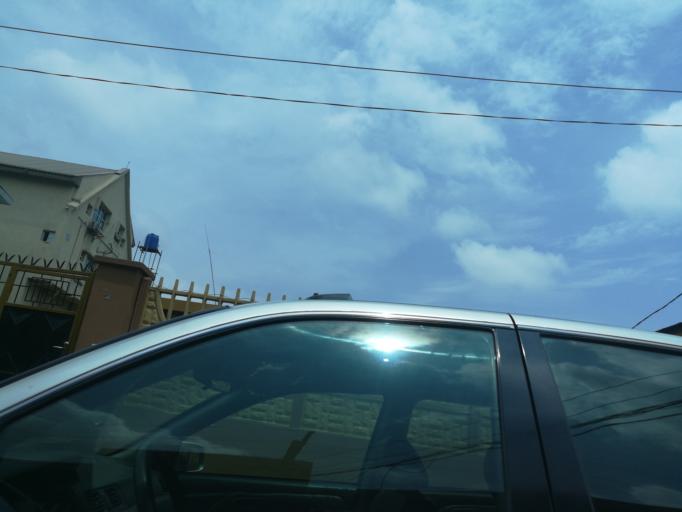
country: NG
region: Lagos
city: Ojota
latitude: 6.5898
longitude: 3.3618
